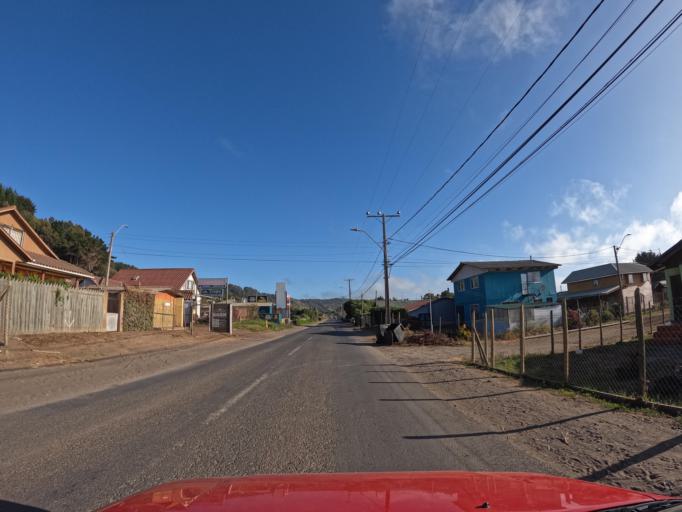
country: CL
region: Maule
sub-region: Provincia de Talca
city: Constitucion
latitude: -34.9237
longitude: -72.1795
